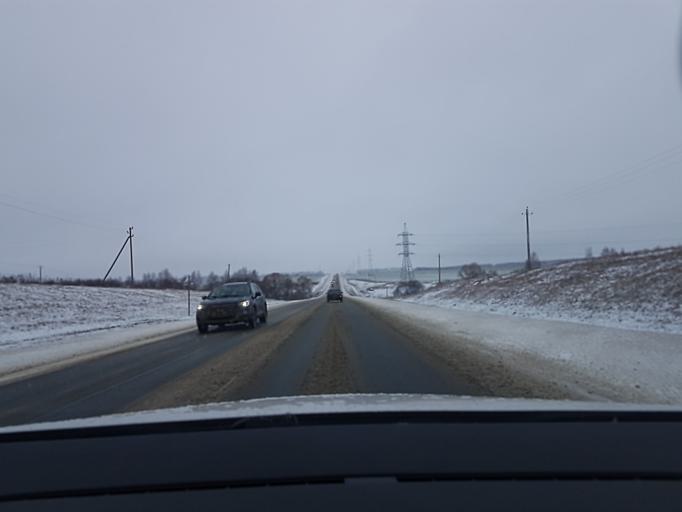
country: RU
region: Rjazan
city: Pavelets
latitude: 54.0645
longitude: 39.2604
